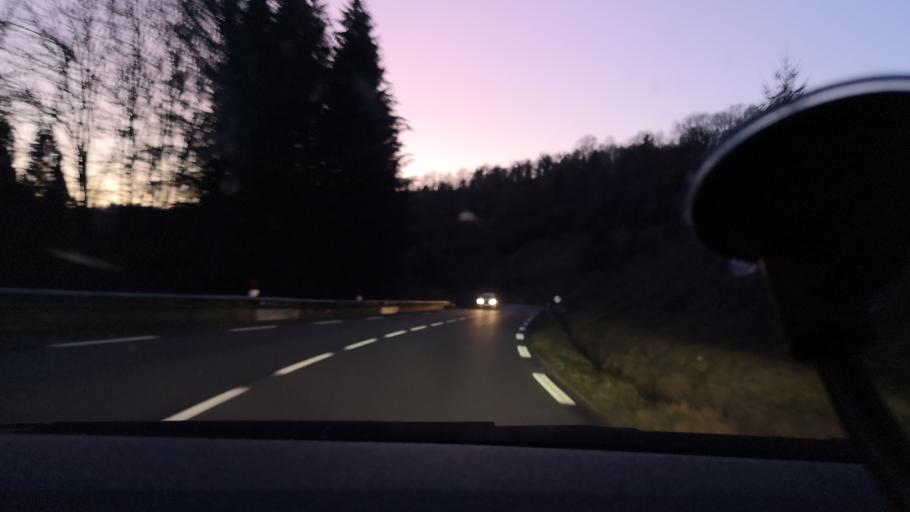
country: FR
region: Franche-Comte
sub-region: Departement du Jura
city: Champagnole
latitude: 46.7730
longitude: 5.9896
